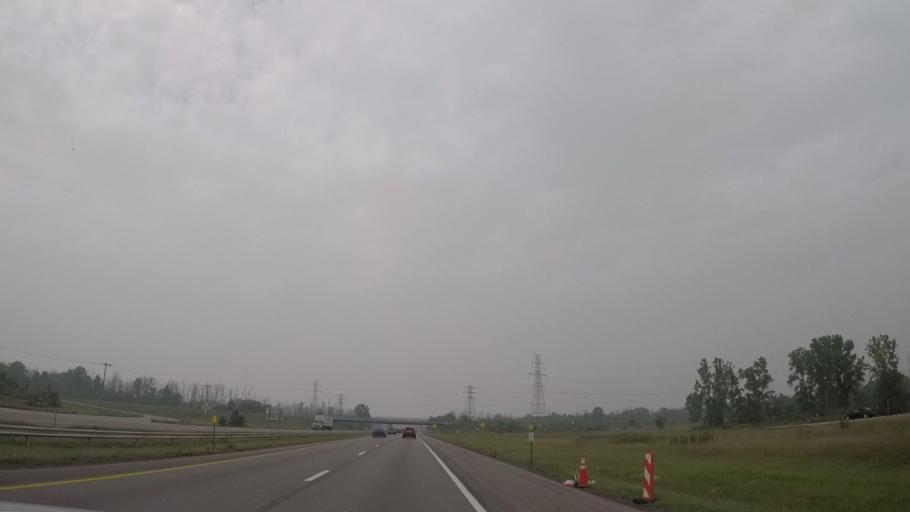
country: US
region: New York
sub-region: Erie County
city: Grandyle Village
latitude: 43.0508
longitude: -78.9904
